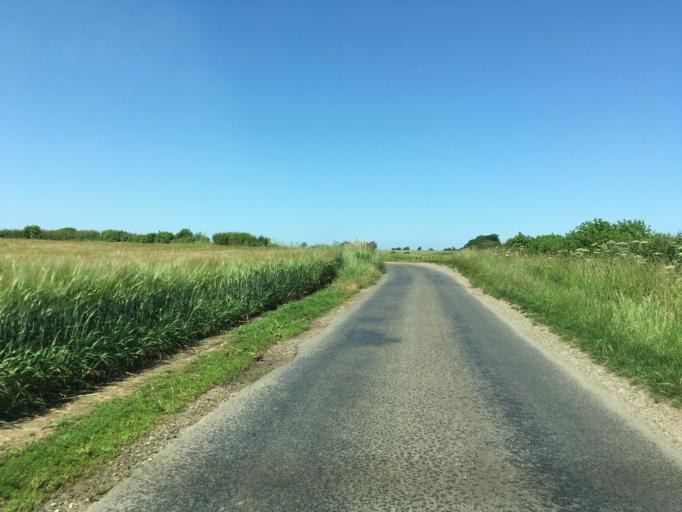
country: GB
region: England
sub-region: Northamptonshire
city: Brackley
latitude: 52.0056
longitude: -1.0908
